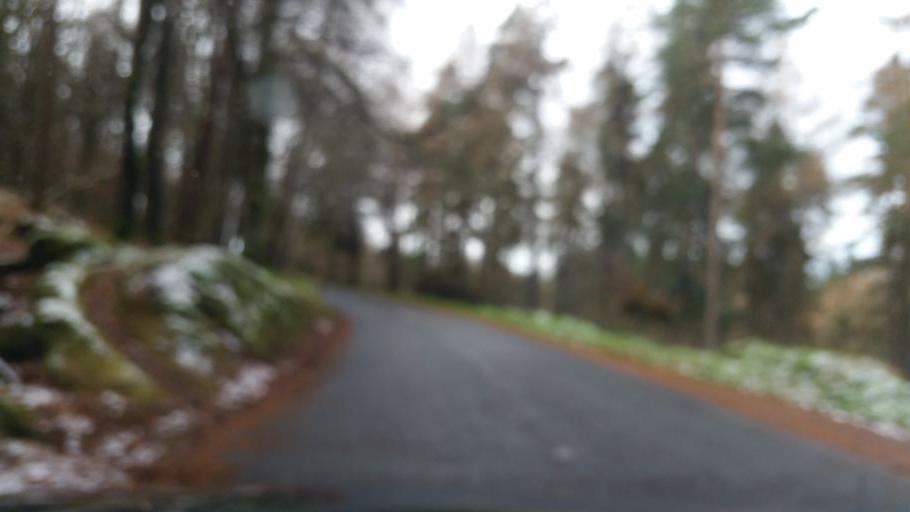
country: IE
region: Leinster
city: Ballyboden
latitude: 53.2436
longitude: -6.3034
